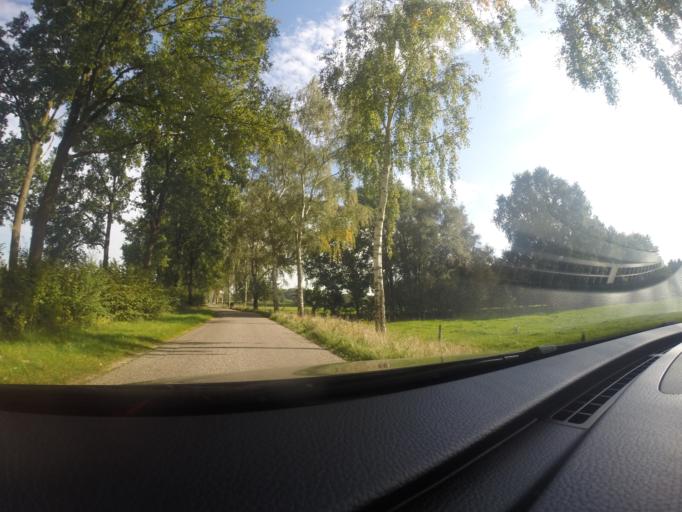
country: NL
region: Gelderland
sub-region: Gemeente Bronckhorst
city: Zelhem
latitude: 51.9745
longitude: 6.3531
